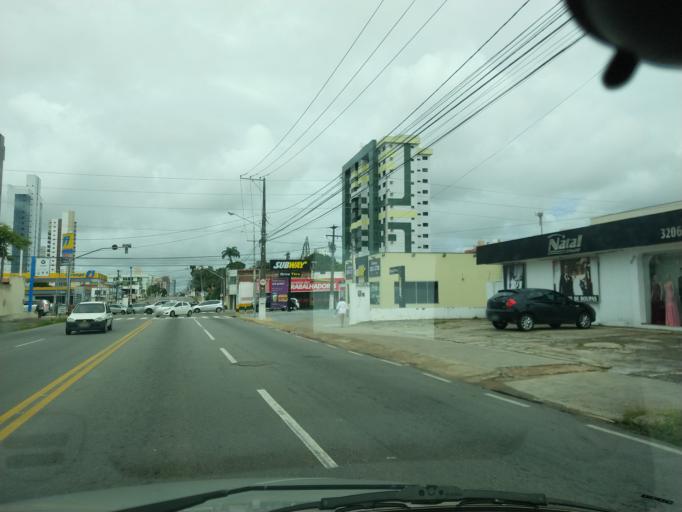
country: BR
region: Rio Grande do Norte
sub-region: Natal
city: Natal
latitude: -5.8167
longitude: -35.2176
